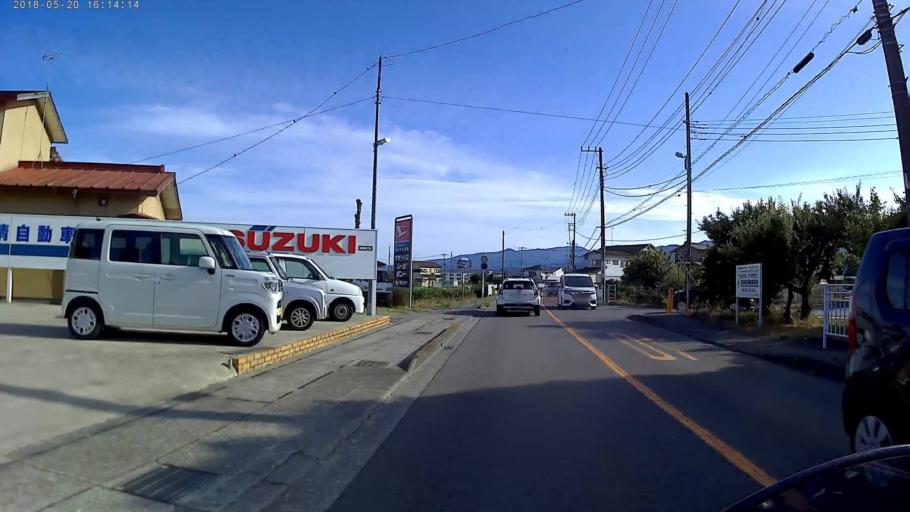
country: JP
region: Kanagawa
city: Odawara
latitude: 35.3156
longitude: 139.1548
